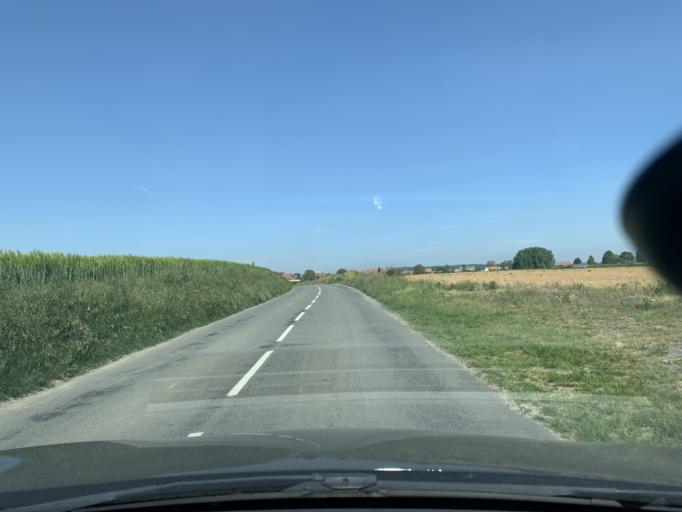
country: FR
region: Nord-Pas-de-Calais
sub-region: Departement du Nord
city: Marcoing
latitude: 50.1445
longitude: 3.1709
